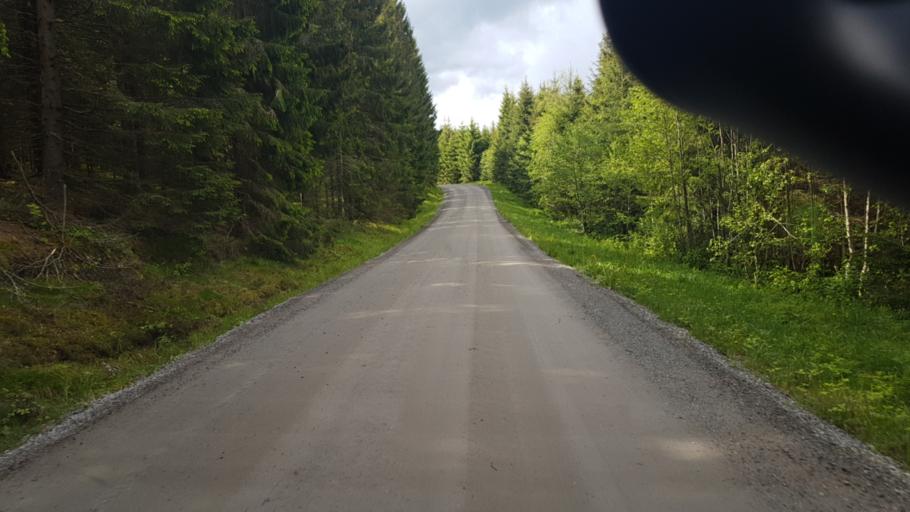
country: NO
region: Ostfold
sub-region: Romskog
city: Romskog
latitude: 59.6958
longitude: 11.9443
